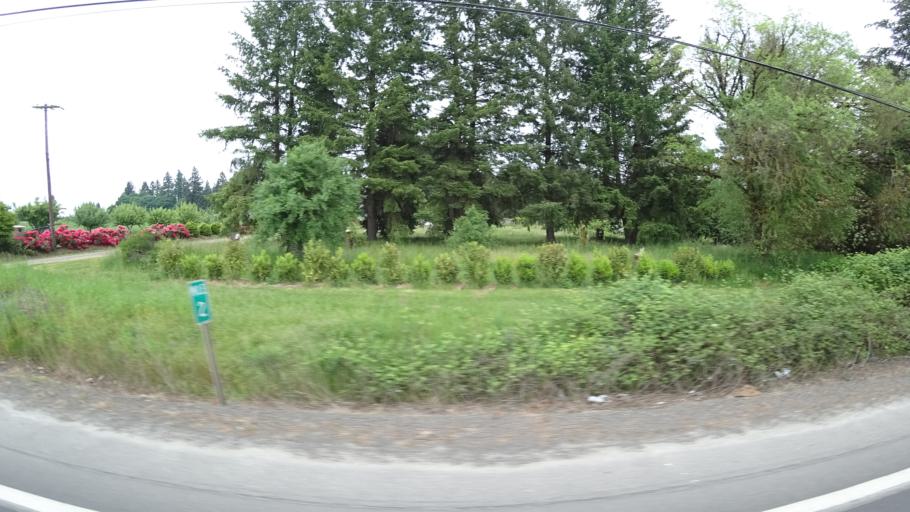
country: US
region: Oregon
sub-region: Washington County
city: Hillsboro
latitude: 45.4906
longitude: -122.9910
